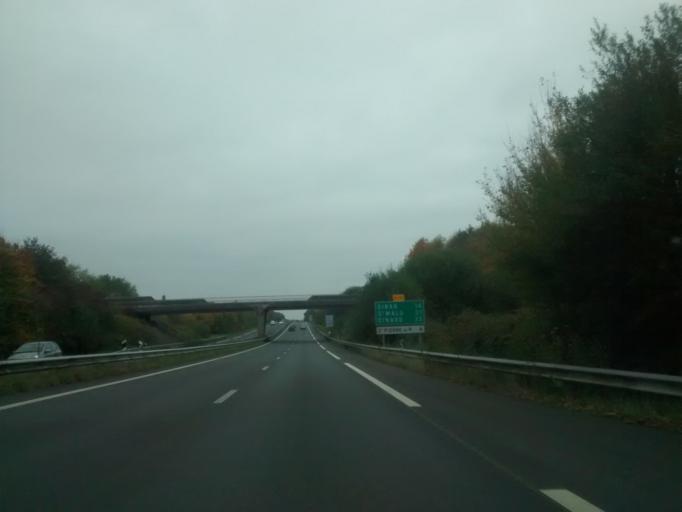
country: FR
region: Brittany
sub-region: Departement d'Ille-et-Vilaine
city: Pleugueneuc
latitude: 48.4173
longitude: -1.9094
